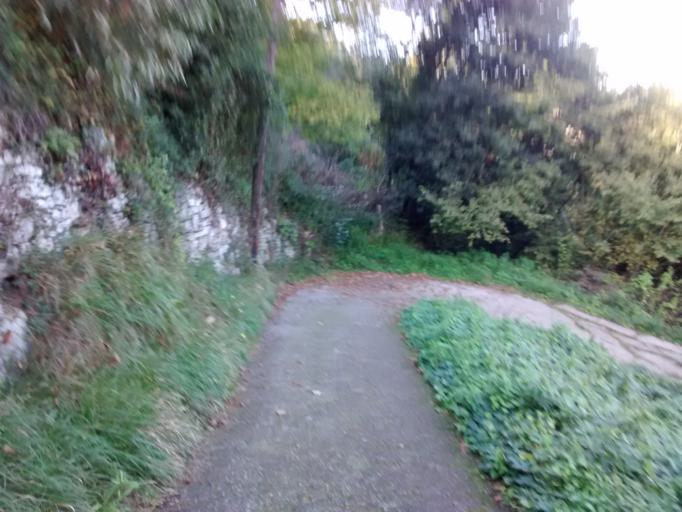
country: ES
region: Asturias
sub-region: Province of Asturias
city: Colunga
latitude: 43.4668
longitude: -5.2299
